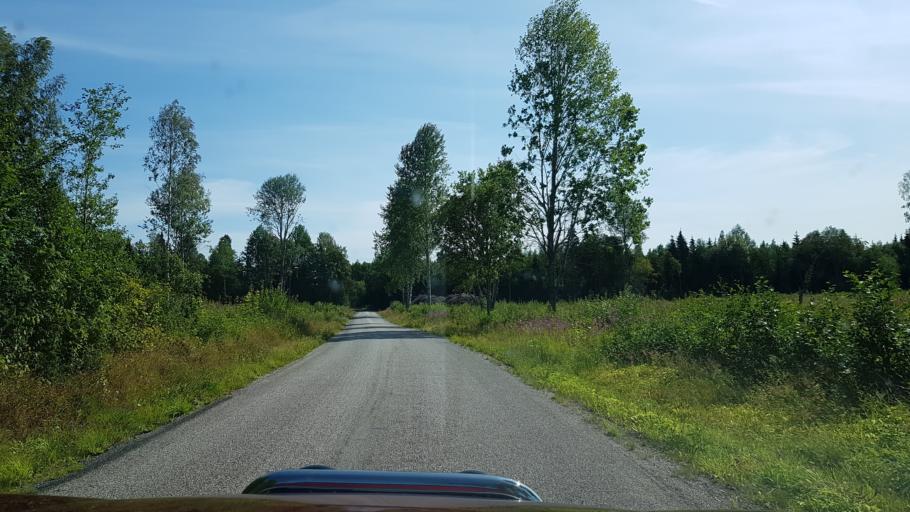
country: EE
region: Jaervamaa
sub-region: Jaerva-Jaani vald
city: Jarva-Jaani
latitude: 59.1174
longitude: 25.6799
